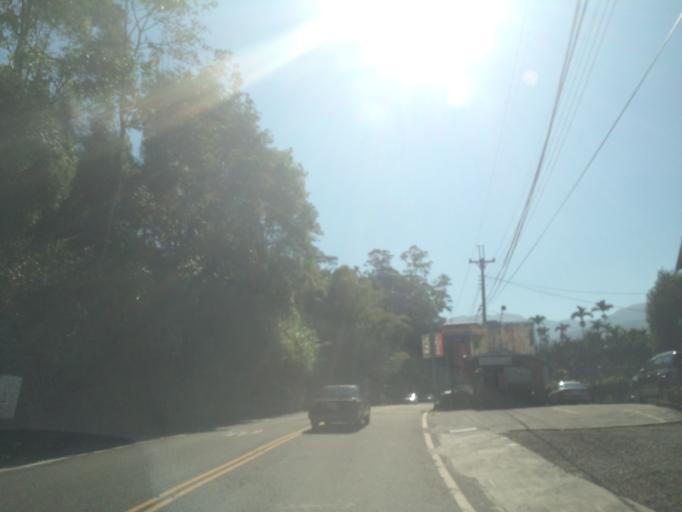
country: TW
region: Taiwan
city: Lugu
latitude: 23.7232
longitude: 120.7777
